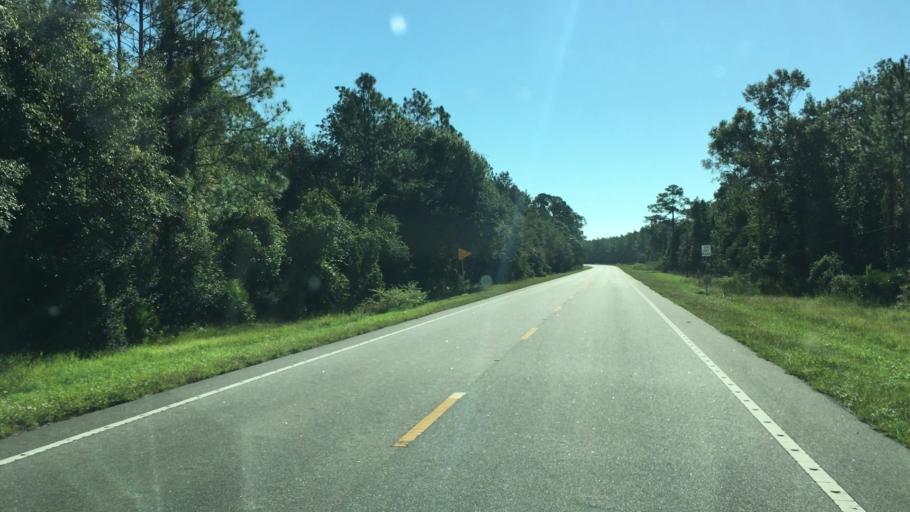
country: US
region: Florida
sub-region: Putnam County
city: Crescent City
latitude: 29.4840
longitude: -81.4582
